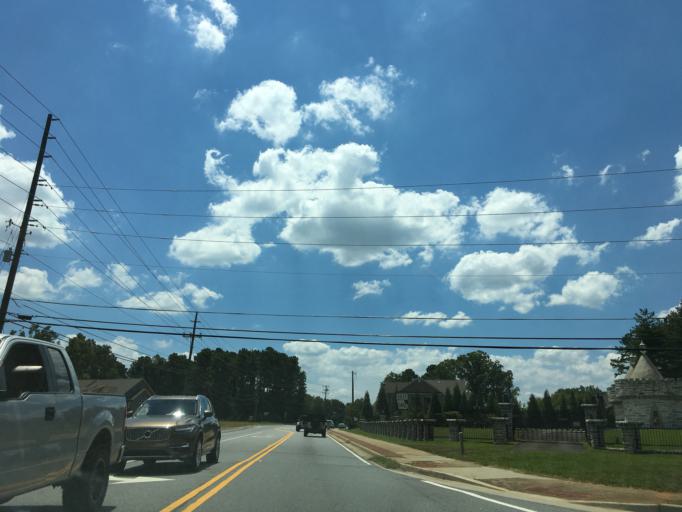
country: US
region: Georgia
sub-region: Fulton County
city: Roswell
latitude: 34.0892
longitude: -84.3610
